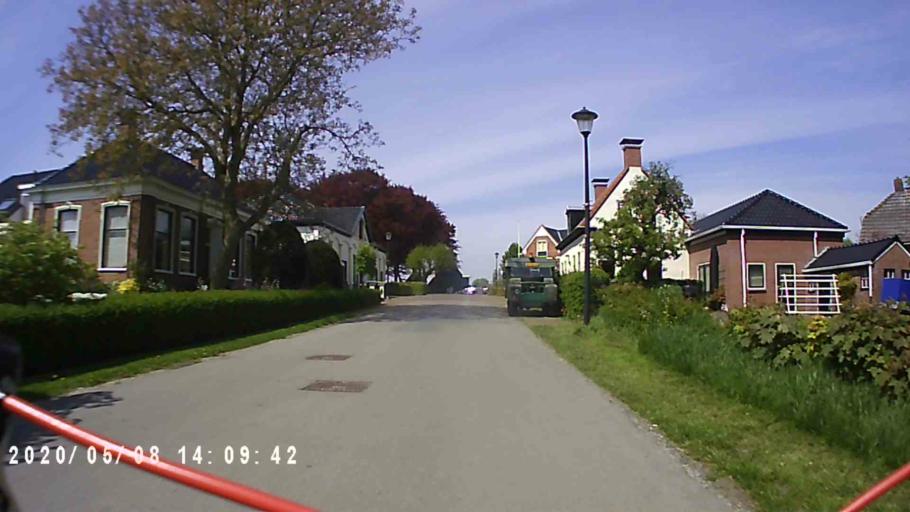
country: NL
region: Groningen
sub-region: Gemeente Appingedam
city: Appingedam
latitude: 53.3455
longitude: 6.7985
